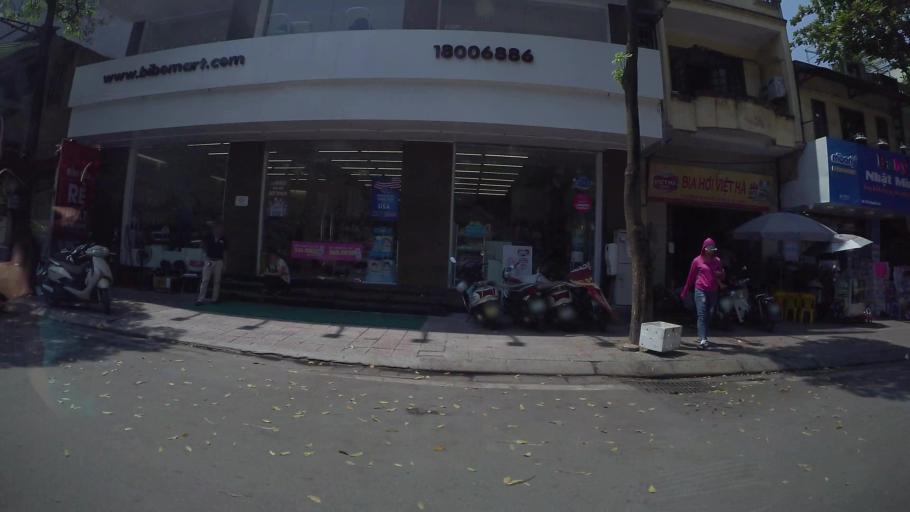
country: VN
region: Ha Noi
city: Hoan Kiem
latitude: 21.0482
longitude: 105.8748
